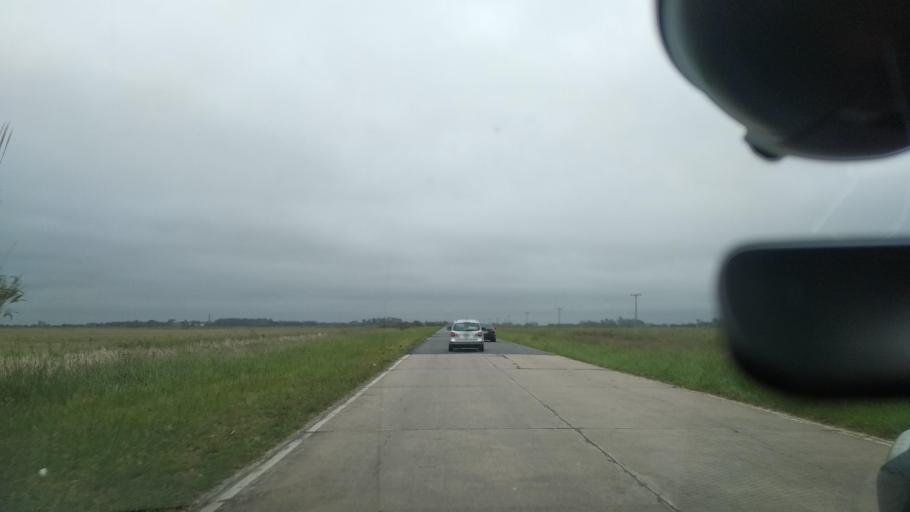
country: AR
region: Buenos Aires
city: Veronica
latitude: -35.5548
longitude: -57.3065
